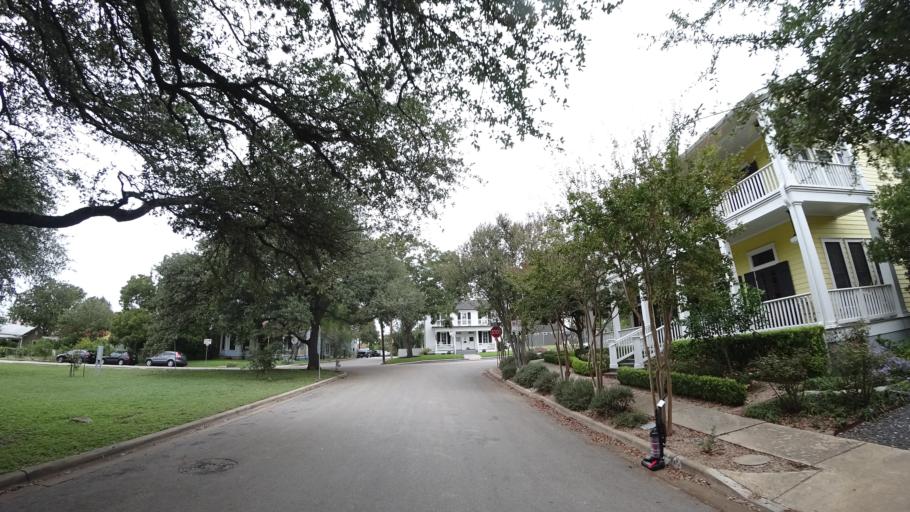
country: US
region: Texas
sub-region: Travis County
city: Austin
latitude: 30.2741
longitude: -97.7293
